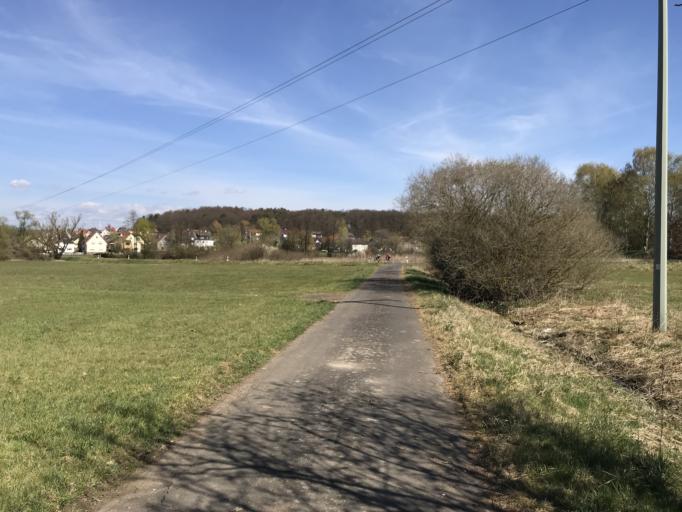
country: DE
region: Hesse
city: Staufenberg
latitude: 50.6419
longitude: 8.7382
